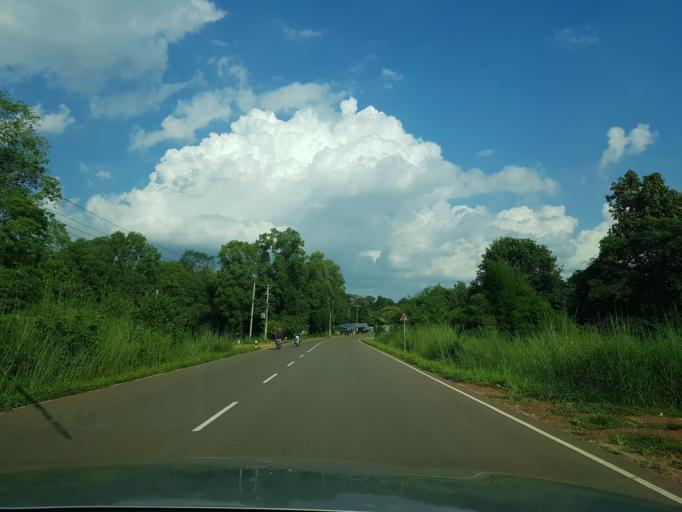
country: TH
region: Nong Khai
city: Pho Tak
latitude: 17.9875
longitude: 102.4344
